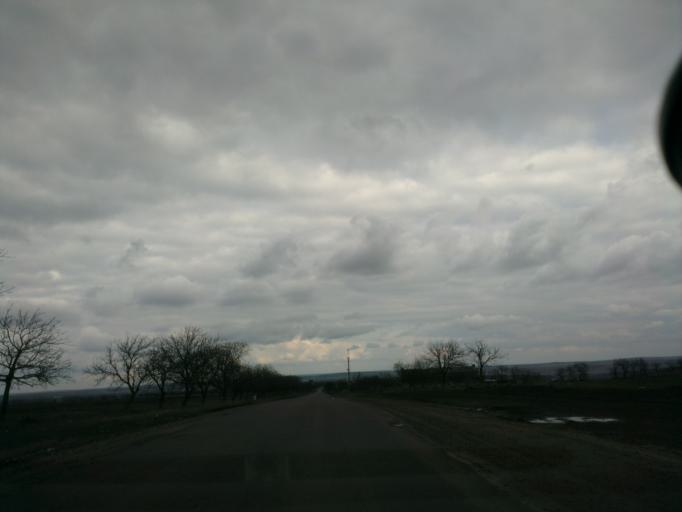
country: MD
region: Gagauzia
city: Comrat
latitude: 46.3083
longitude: 28.6072
